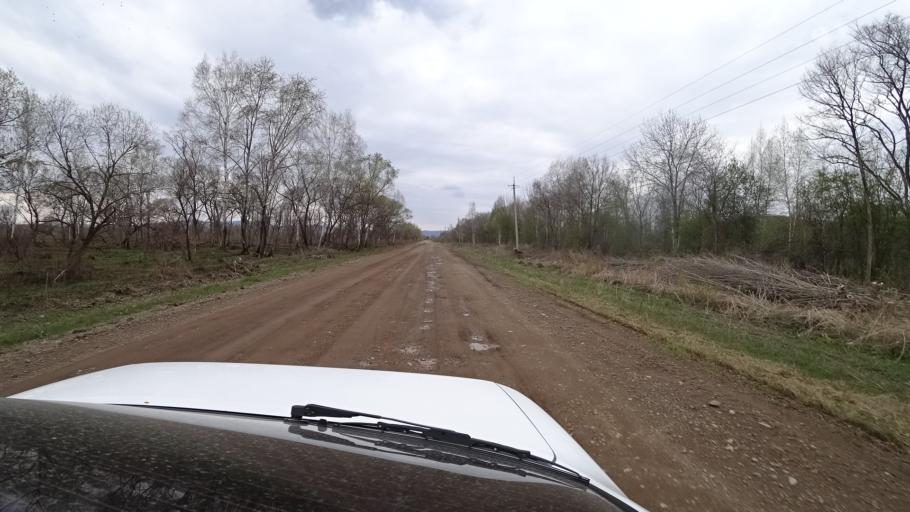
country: RU
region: Primorskiy
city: Novopokrovka
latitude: 45.5594
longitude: 134.3470
